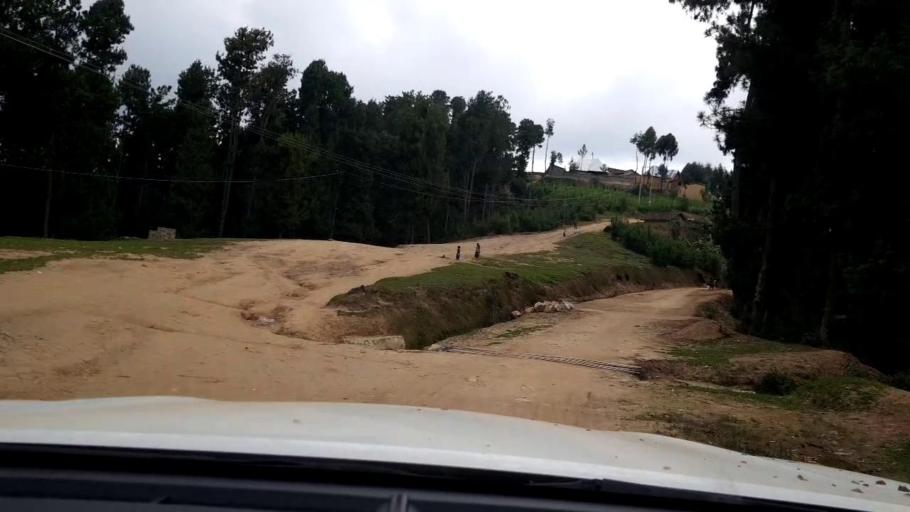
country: RW
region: Western Province
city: Kibuye
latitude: -1.8923
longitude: 29.5278
